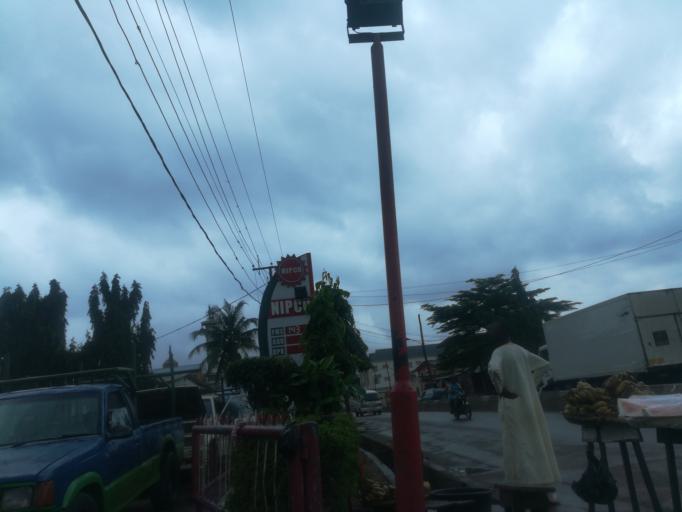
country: NG
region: Lagos
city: Agege
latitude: 6.6261
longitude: 3.3099
